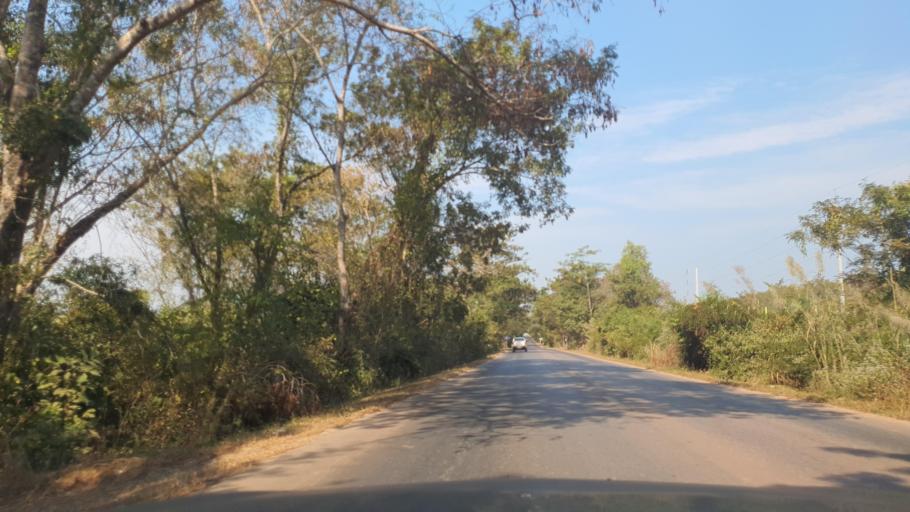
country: TH
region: Nakhon Phanom
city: Ban Phaeng
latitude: 18.0188
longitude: 104.1523
